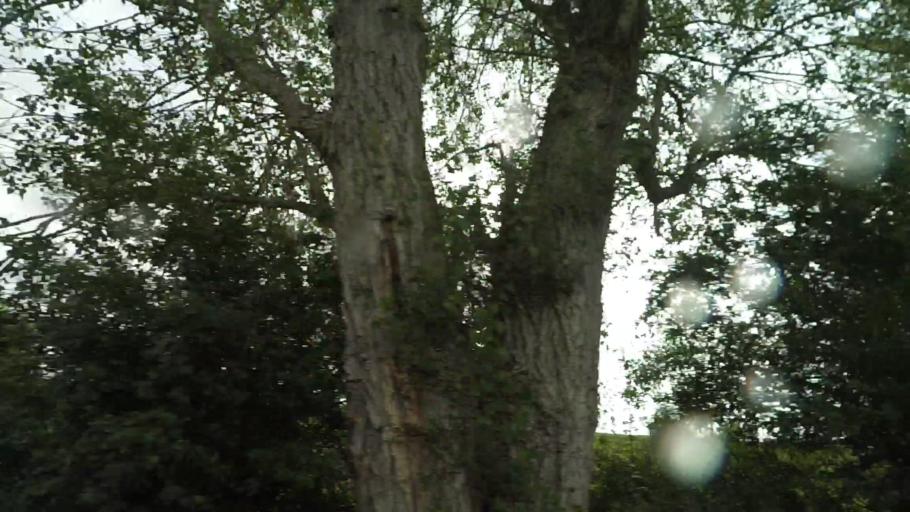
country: DK
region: Central Jutland
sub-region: Syddjurs Kommune
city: Ronde
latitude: 56.2980
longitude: 10.4445
